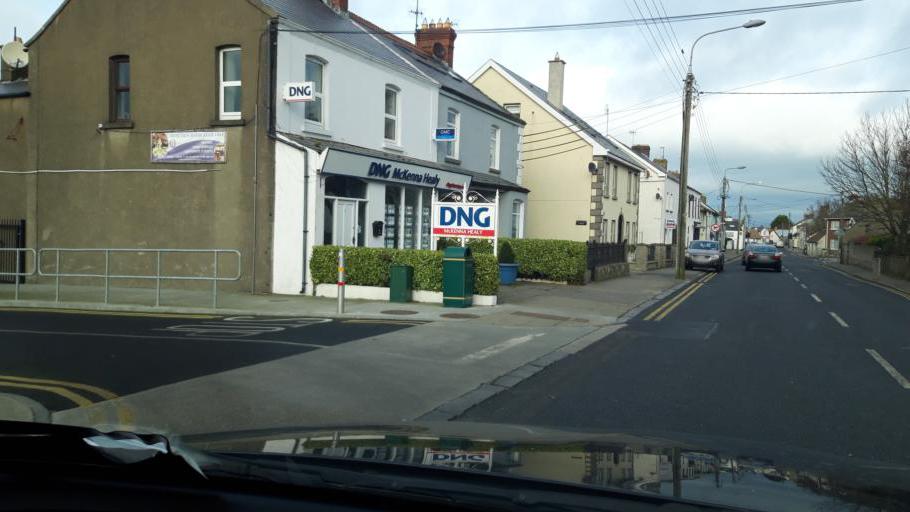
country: IE
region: Leinster
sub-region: Fingal County
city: Skerries
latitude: 53.5780
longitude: -6.1119
